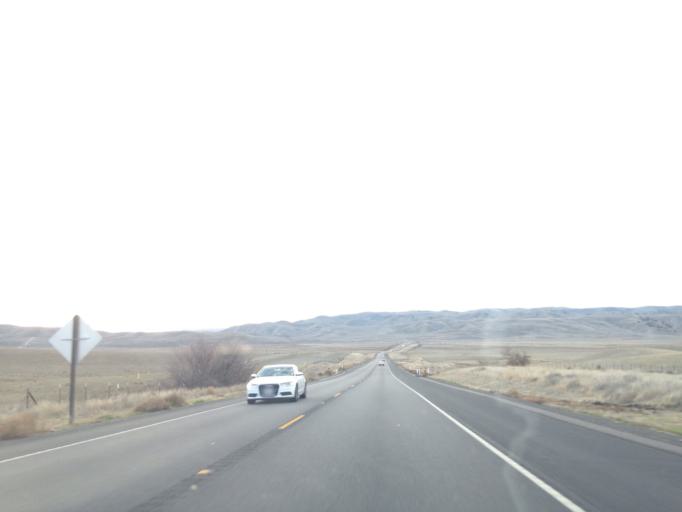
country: US
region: California
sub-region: San Luis Obispo County
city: Shandon
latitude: 35.7393
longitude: -120.2615
